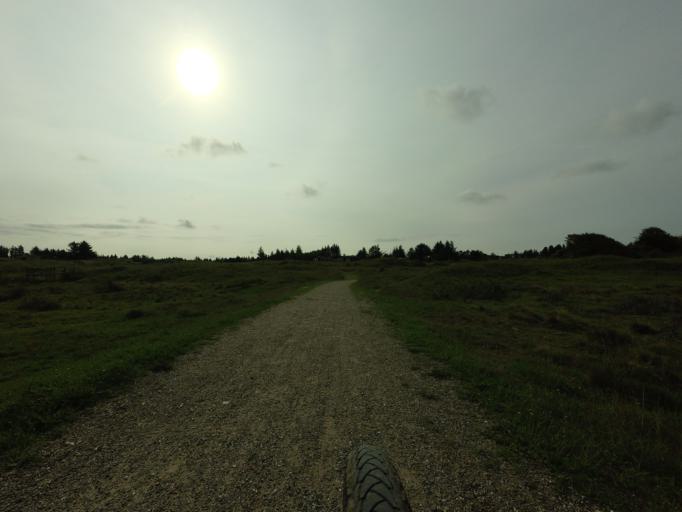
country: DK
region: North Denmark
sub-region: Hjorring Kommune
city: Sindal
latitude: 57.5883
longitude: 10.1476
